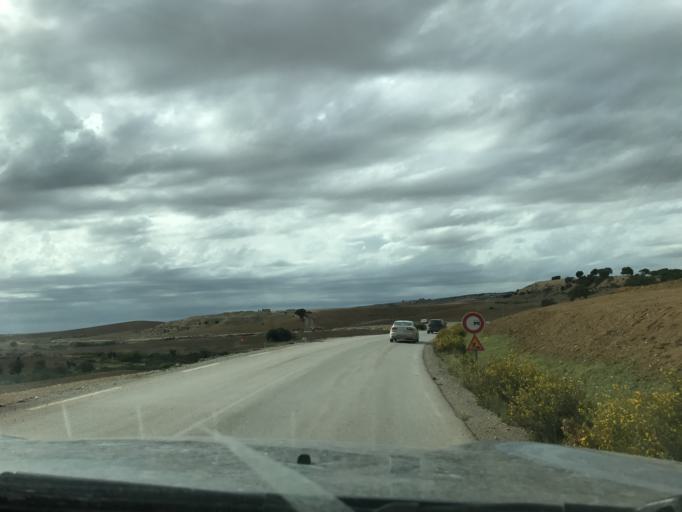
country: TN
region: Silyanah
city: Bu `Aradah
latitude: 36.1809
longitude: 9.6722
